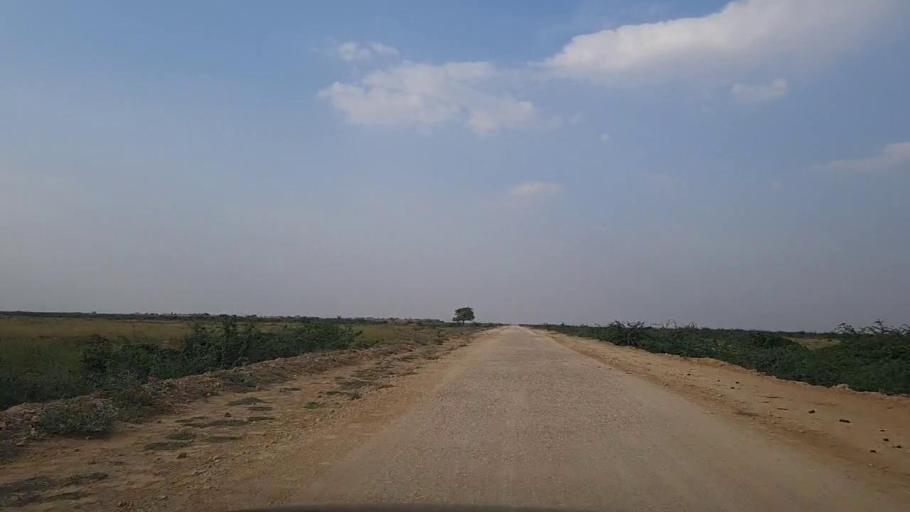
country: PK
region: Sindh
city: Gharo
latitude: 24.8269
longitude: 67.7452
